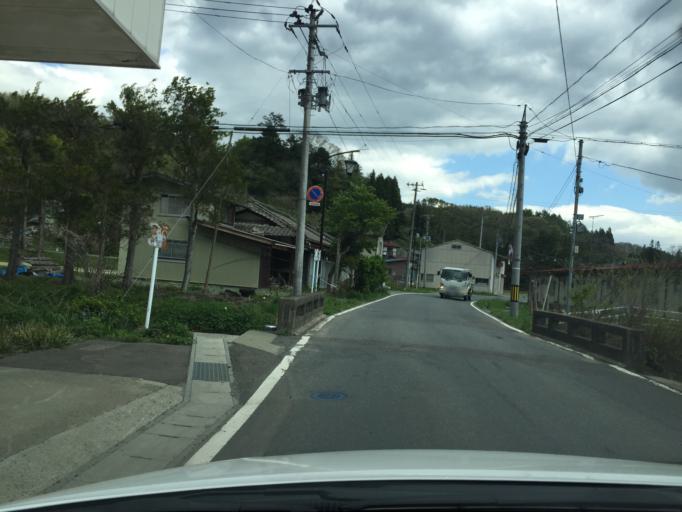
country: JP
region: Fukushima
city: Yanagawamachi-saiwaicho
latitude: 37.6963
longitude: 140.7569
